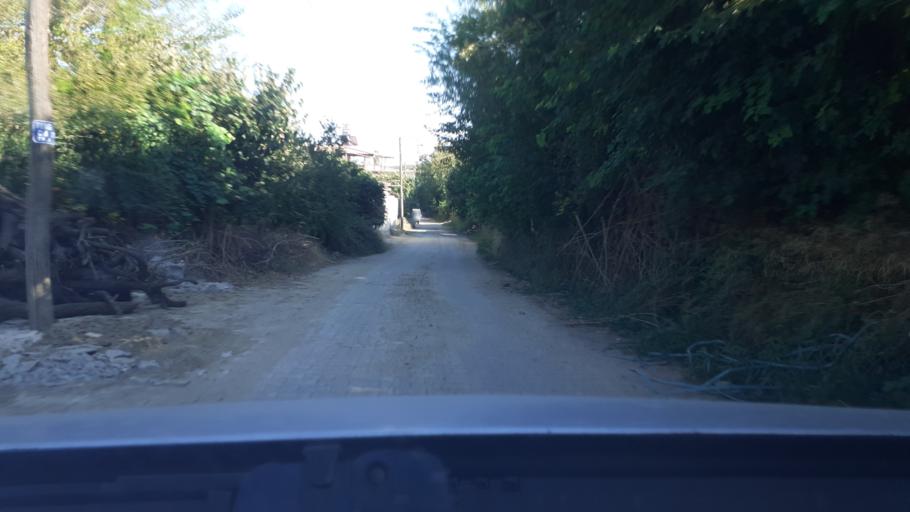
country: TR
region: Hatay
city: Kirikhan
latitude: 36.4886
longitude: 36.3003
